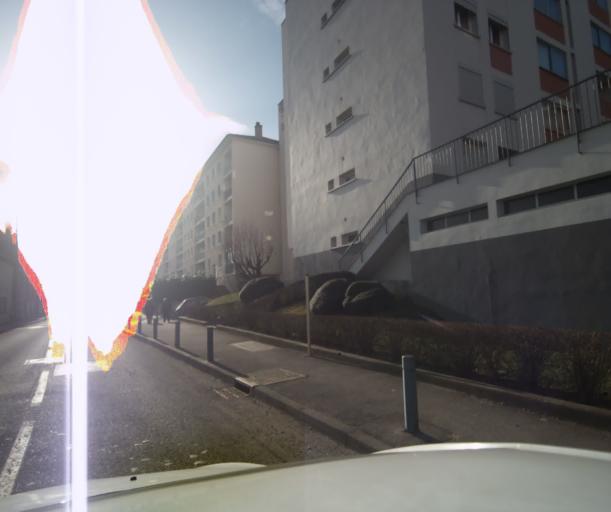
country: FR
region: Franche-Comte
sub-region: Departement du Doubs
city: Besancon
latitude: 47.2553
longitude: 6.0433
